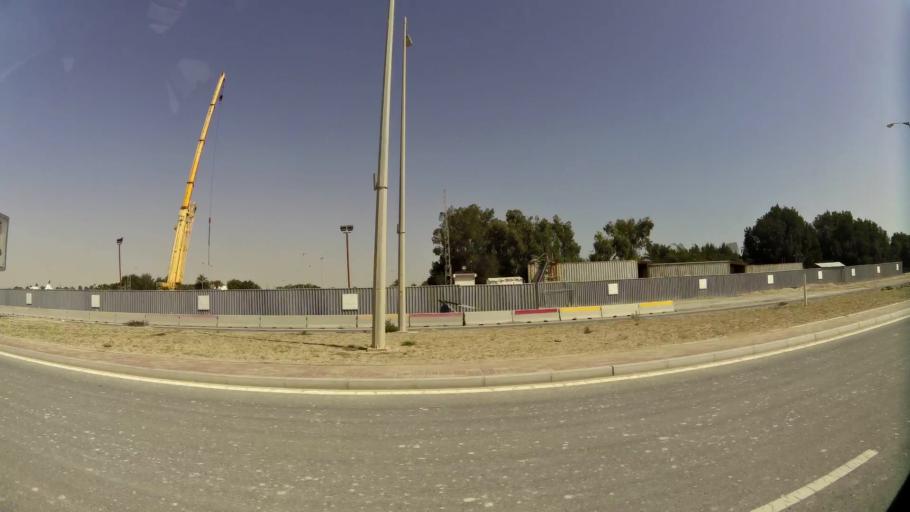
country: QA
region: Baladiyat ad Dawhah
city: Doha
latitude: 25.3774
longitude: 51.5072
